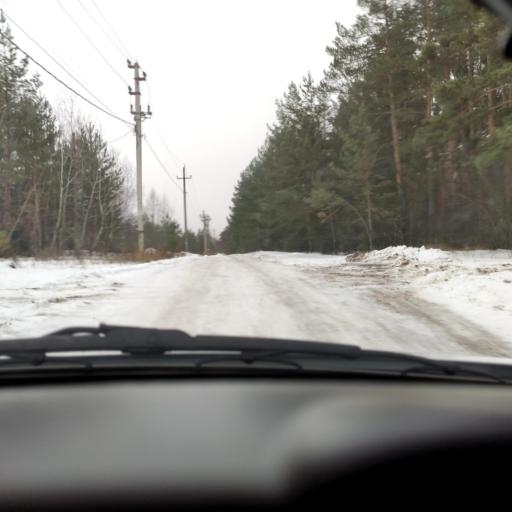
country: RU
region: Voronezj
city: Ramon'
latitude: 51.8859
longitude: 39.2557
